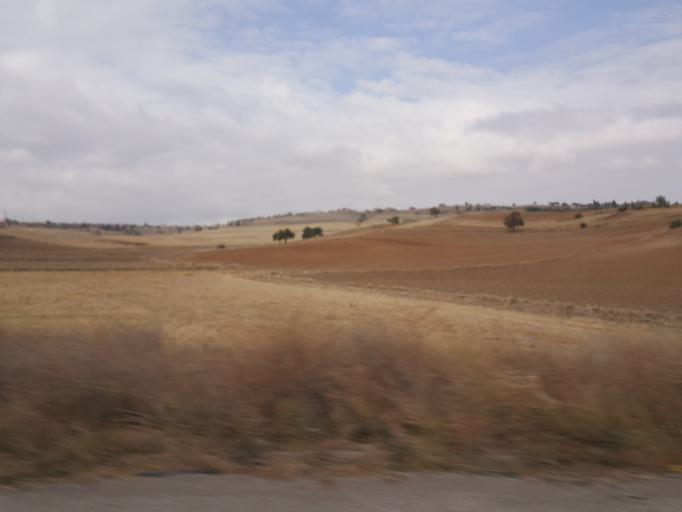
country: TR
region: Kirikkale
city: Karakecili
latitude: 39.6185
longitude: 33.4236
